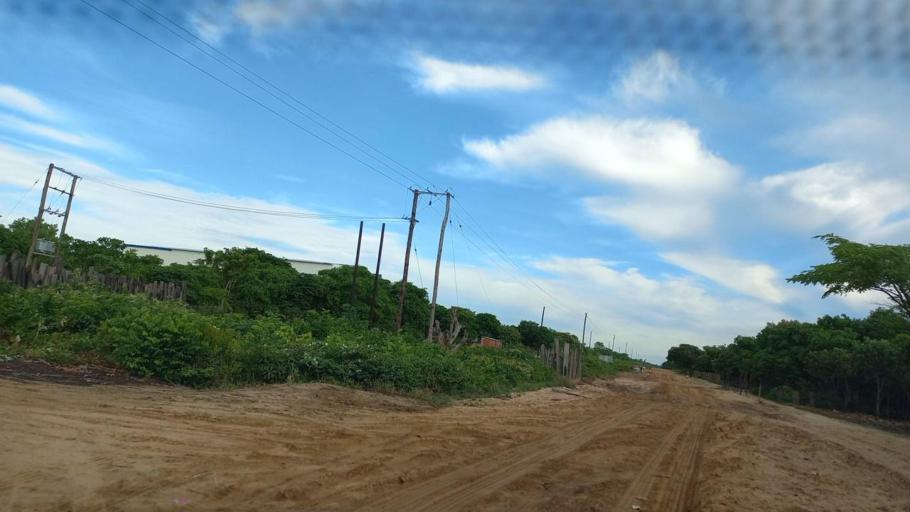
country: ZM
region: North-Western
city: Kabompo
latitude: -13.4146
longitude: 24.3183
